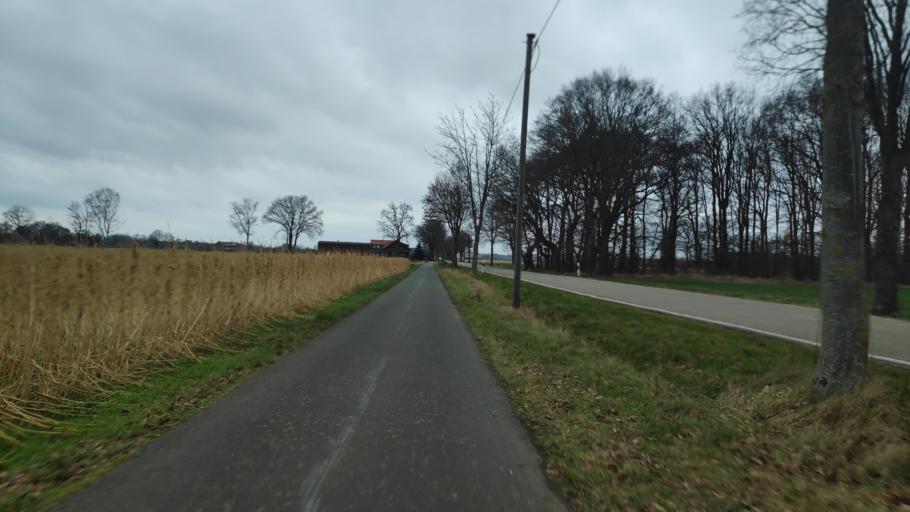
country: DE
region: North Rhine-Westphalia
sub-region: Regierungsbezirk Detmold
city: Hille
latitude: 52.3598
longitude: 8.7823
